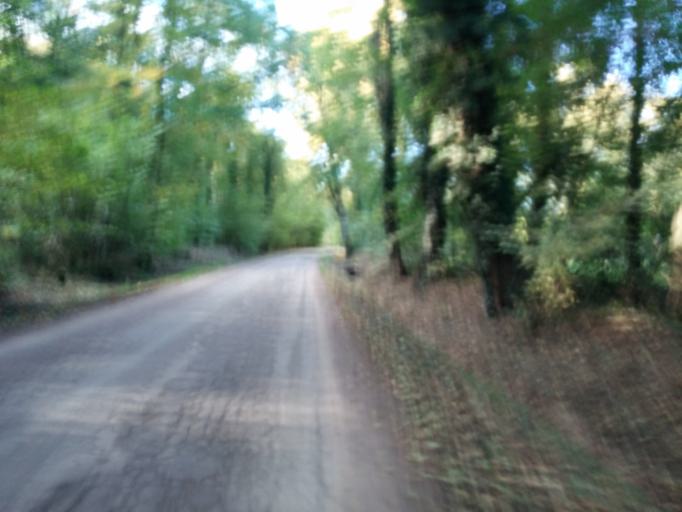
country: DE
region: North Rhine-Westphalia
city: Dorsten
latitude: 51.6216
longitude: 6.9953
